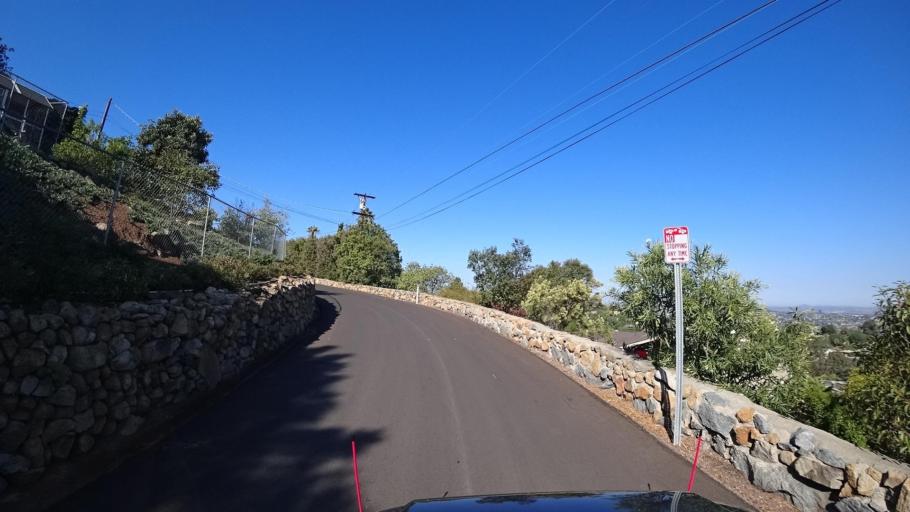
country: US
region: California
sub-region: San Diego County
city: Casa de Oro-Mount Helix
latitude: 32.7710
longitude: -116.9814
